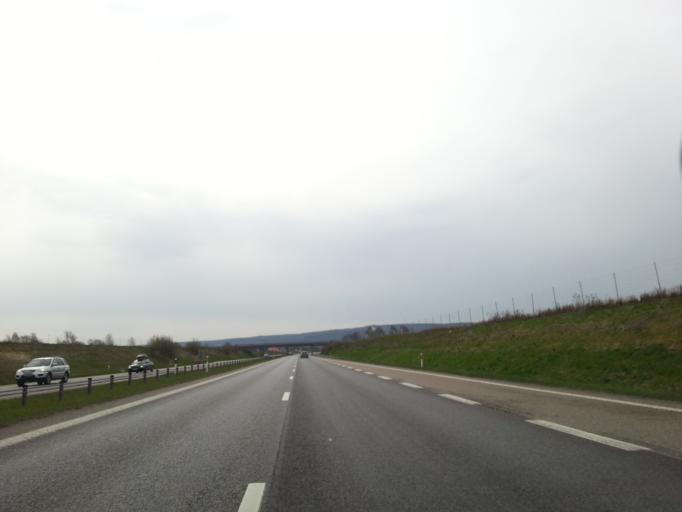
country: SE
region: Halland
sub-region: Laholms Kommun
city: Mellbystrand
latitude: 56.4517
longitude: 12.9493
